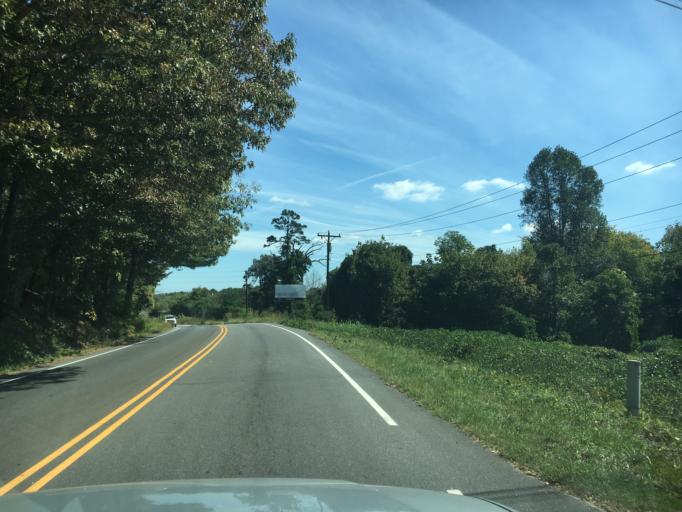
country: US
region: North Carolina
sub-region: Rutherford County
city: Rutherfordton
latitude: 35.3827
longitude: -81.9516
